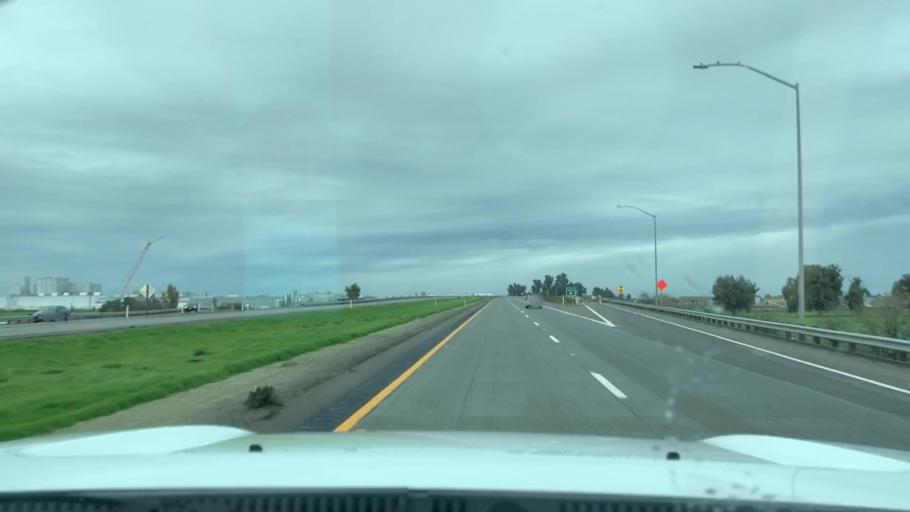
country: US
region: California
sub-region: Kings County
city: Lemoore
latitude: 36.2933
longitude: -119.8094
